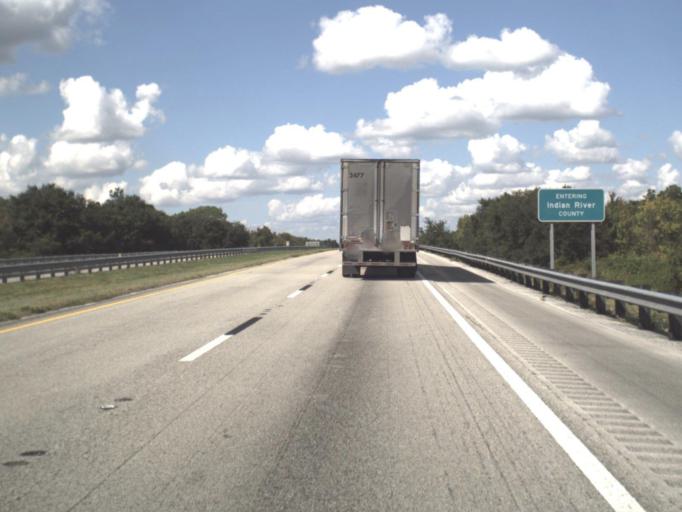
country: US
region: Florida
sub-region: Indian River County
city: Fellsmere
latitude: 27.6425
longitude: -80.8529
